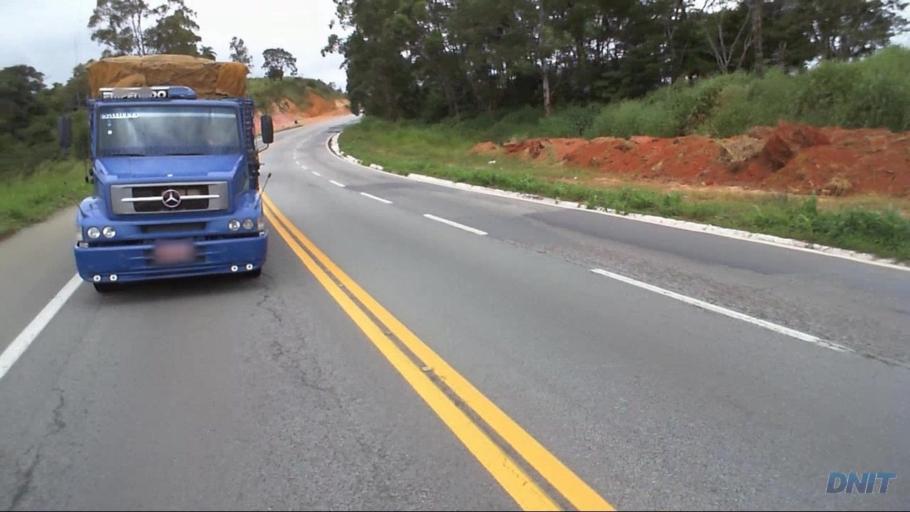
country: BR
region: Minas Gerais
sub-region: Caete
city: Caete
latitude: -19.7295
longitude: -43.5608
